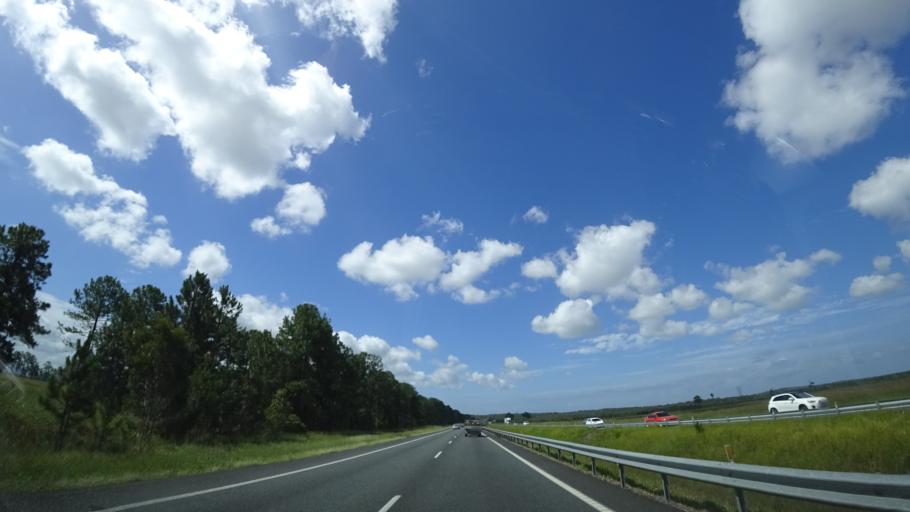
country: AU
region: Queensland
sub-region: Sunshine Coast
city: Little Mountain
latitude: -26.8222
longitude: 153.0356
